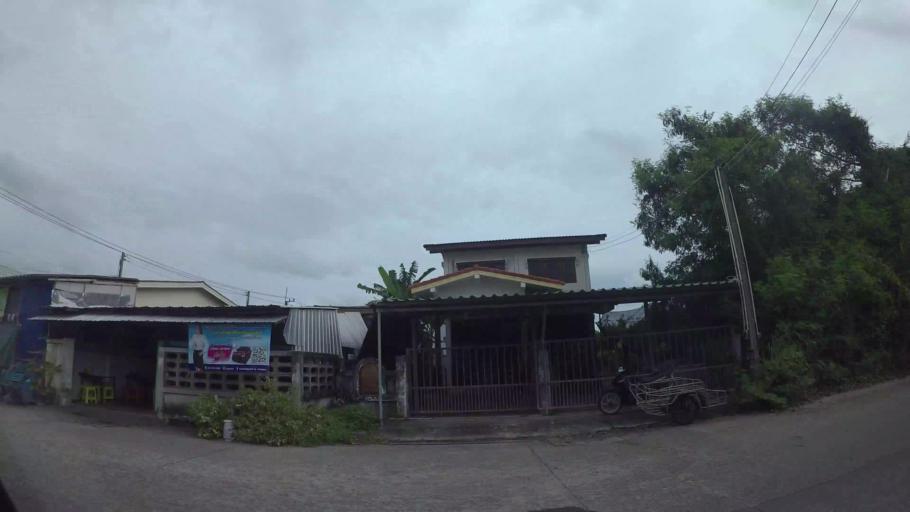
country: TH
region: Rayong
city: Rayong
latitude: 12.6711
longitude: 101.2774
